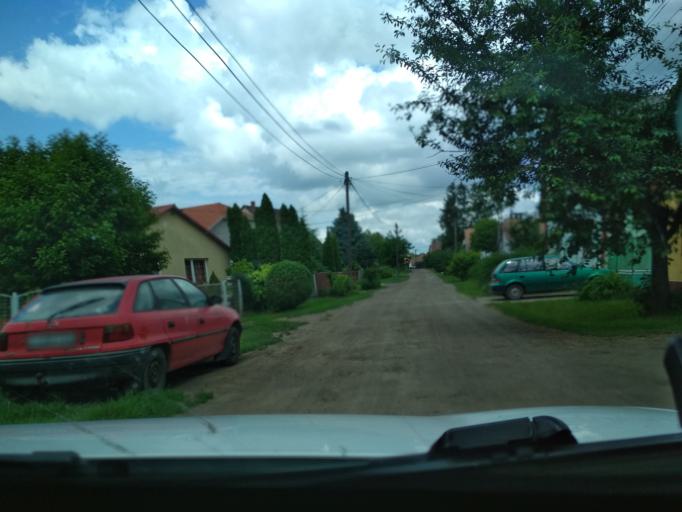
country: HU
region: Jasz-Nagykun-Szolnok
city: Tiszafured
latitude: 47.6102
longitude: 20.7467
